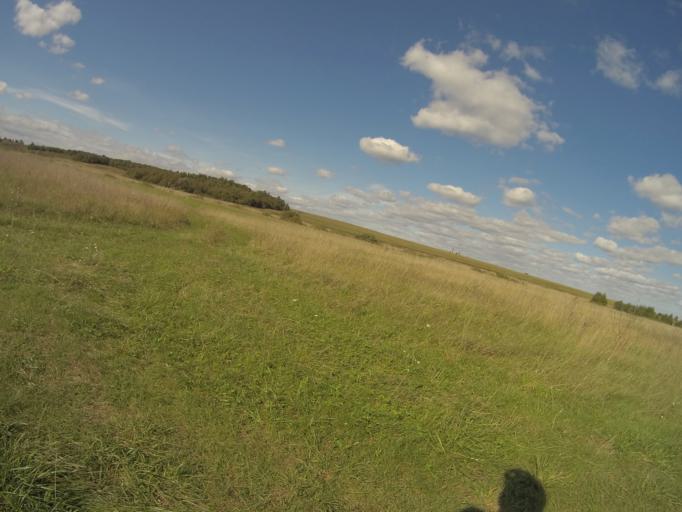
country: RU
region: Vladimir
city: Orgtrud
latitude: 56.3064
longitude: 40.6332
